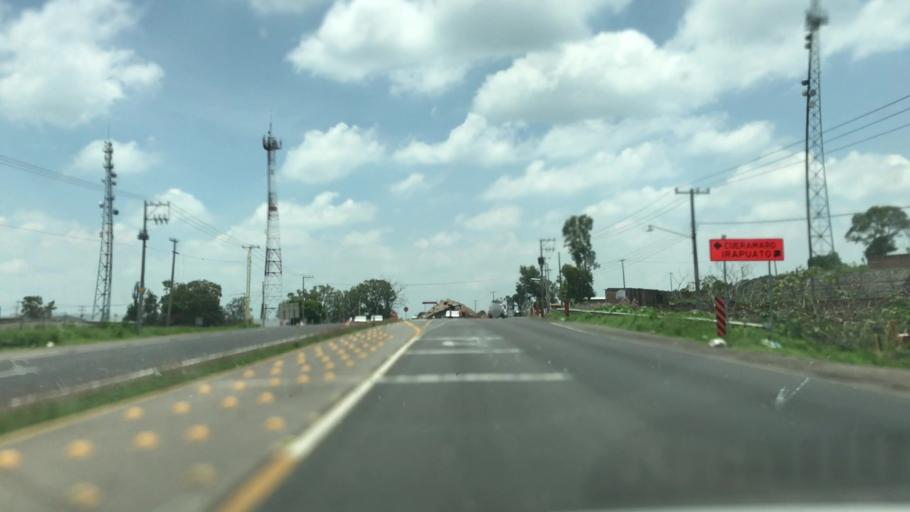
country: MX
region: Guanajuato
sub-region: Irapuato
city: San Ignacio de Rivera (Ojo de Agua)
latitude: 20.5616
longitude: -101.4487
